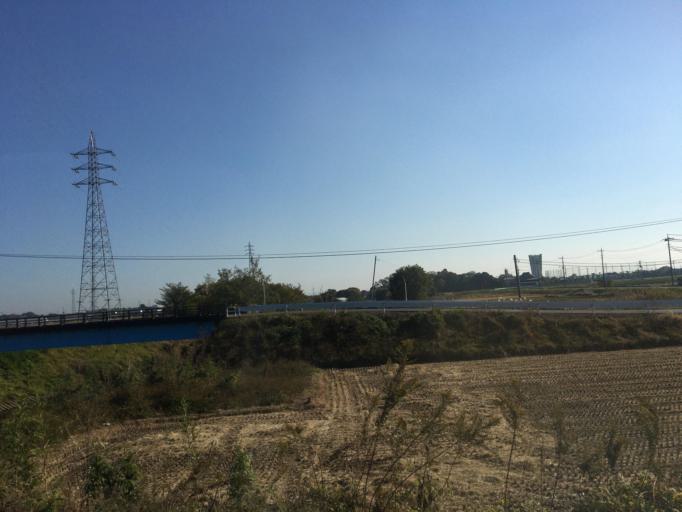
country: JP
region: Gunma
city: Tatebayashi
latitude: 36.2178
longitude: 139.5268
